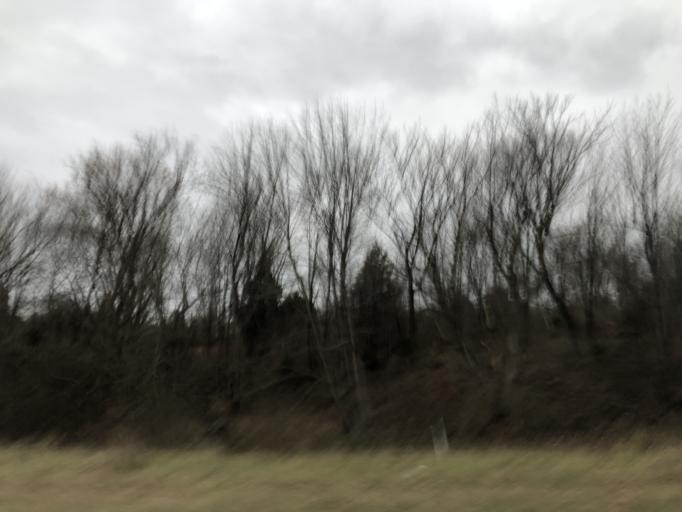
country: US
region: Illinois
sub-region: Johnson County
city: Vienna
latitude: 37.3527
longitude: -88.7884
